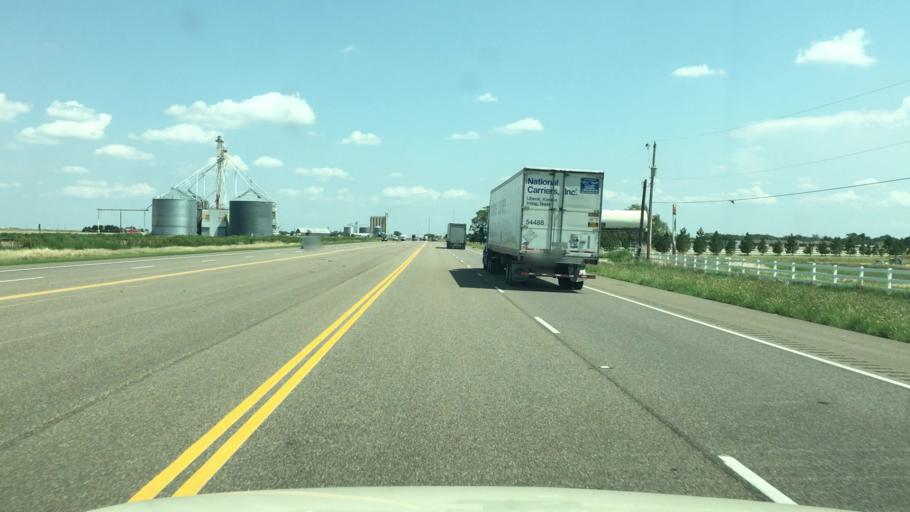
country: US
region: Texas
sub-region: Armstrong County
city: Claude
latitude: 35.1181
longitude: -101.3776
